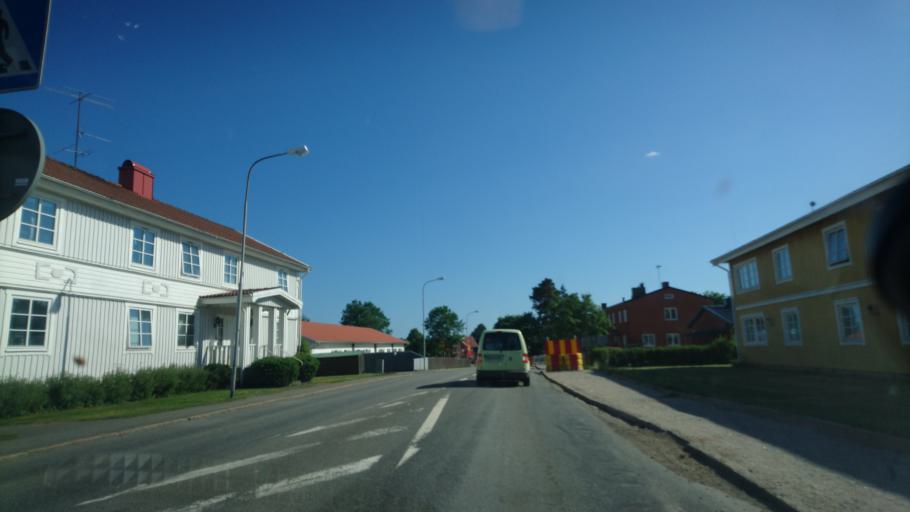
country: SE
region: Skane
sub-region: Osby Kommun
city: Lonsboda
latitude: 56.4009
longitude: 14.3191
